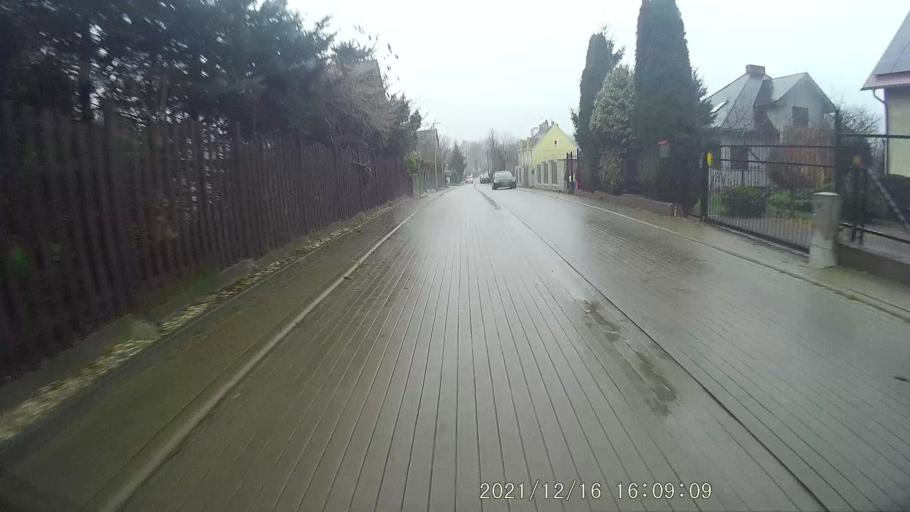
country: PL
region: Lower Silesian Voivodeship
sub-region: Powiat zgorzelecki
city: Lagow
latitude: 51.1562
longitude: 15.0399
